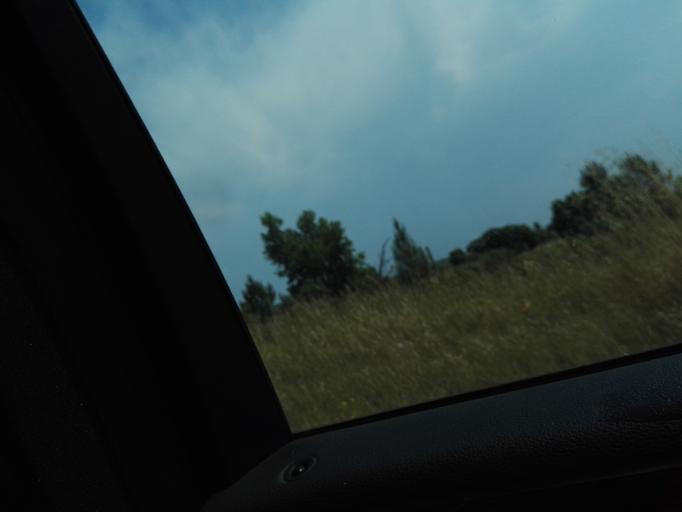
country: PT
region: Santarem
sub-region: Entroncamento
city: Entroncamento
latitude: 39.4702
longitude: -8.4574
